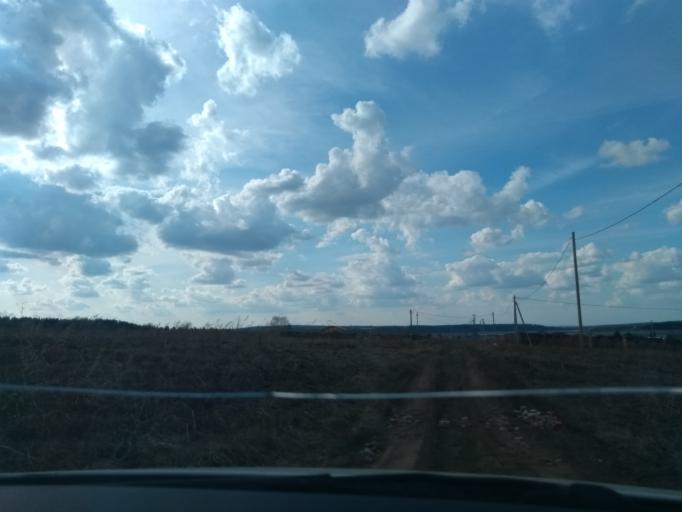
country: RU
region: Perm
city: Sylva
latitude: 57.8444
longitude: 56.7883
